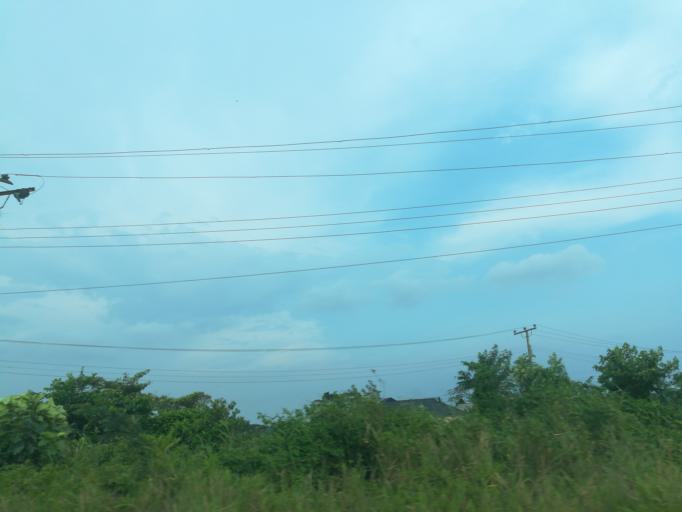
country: NG
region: Lagos
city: Ikorodu
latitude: 6.6398
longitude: 3.6702
